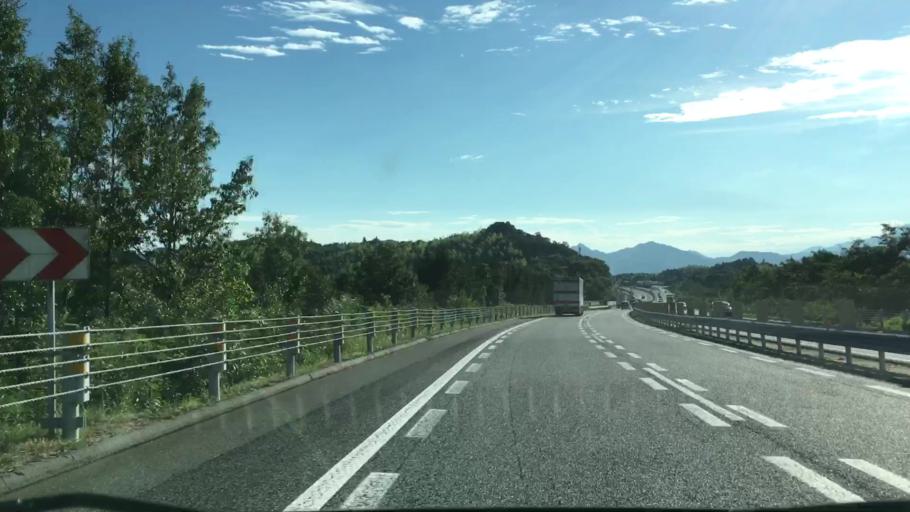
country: JP
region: Yamaguchi
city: Iwakuni
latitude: 34.1037
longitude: 132.1105
